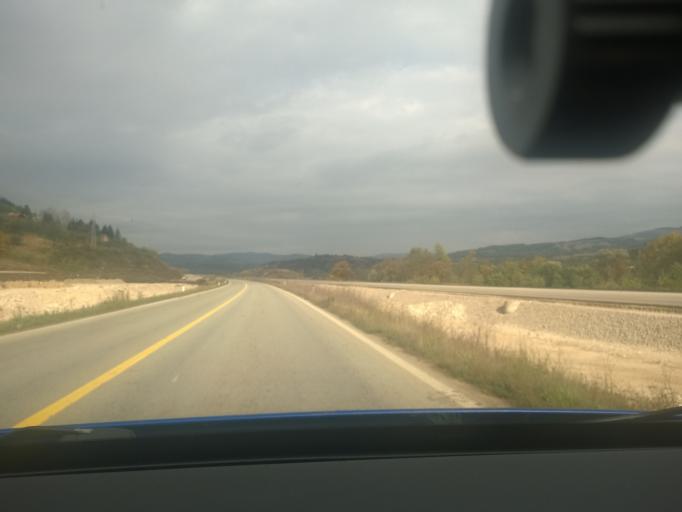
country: RS
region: Central Serbia
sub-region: Pirotski Okrug
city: Pirot
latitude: 43.2034
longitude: 22.5565
